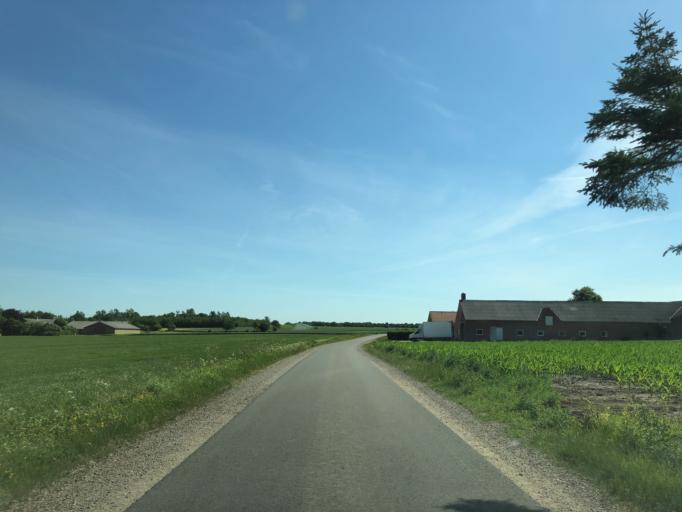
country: DK
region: Central Jutland
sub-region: Struer Kommune
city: Struer
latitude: 56.4308
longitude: 8.4691
